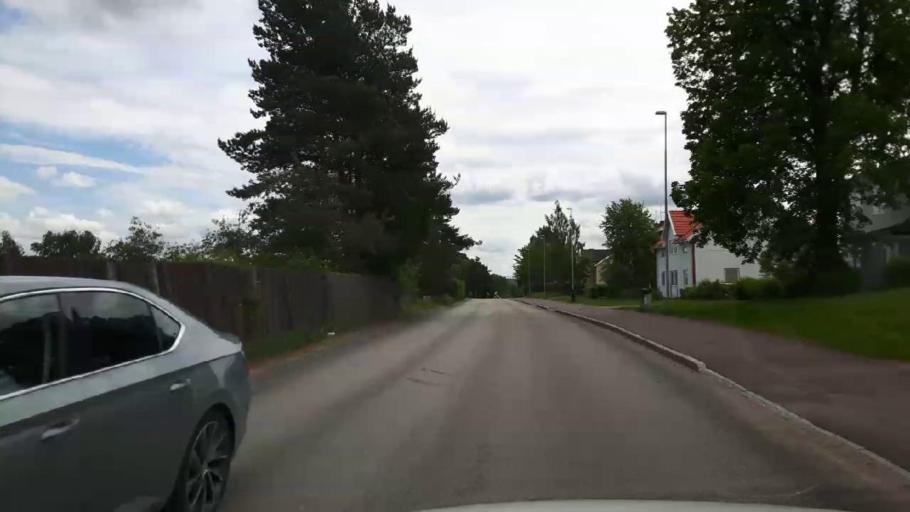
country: SE
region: Dalarna
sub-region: Hedemora Kommun
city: Hedemora
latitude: 60.2709
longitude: 15.9935
